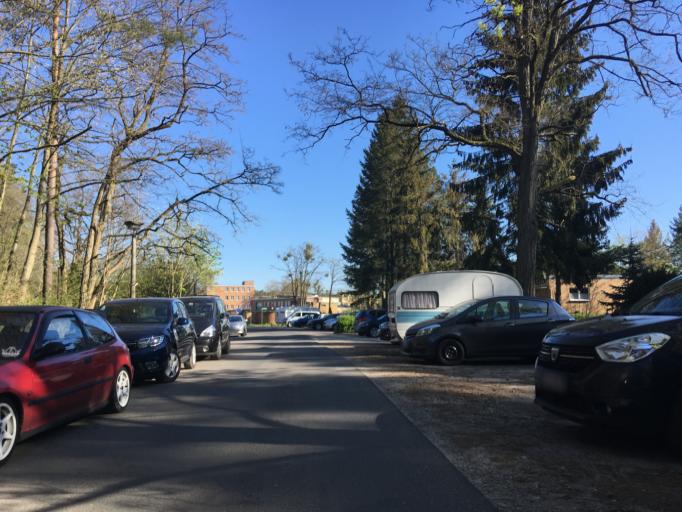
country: DE
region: Brandenburg
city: Bernau bei Berlin
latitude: 52.7045
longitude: 13.5441
